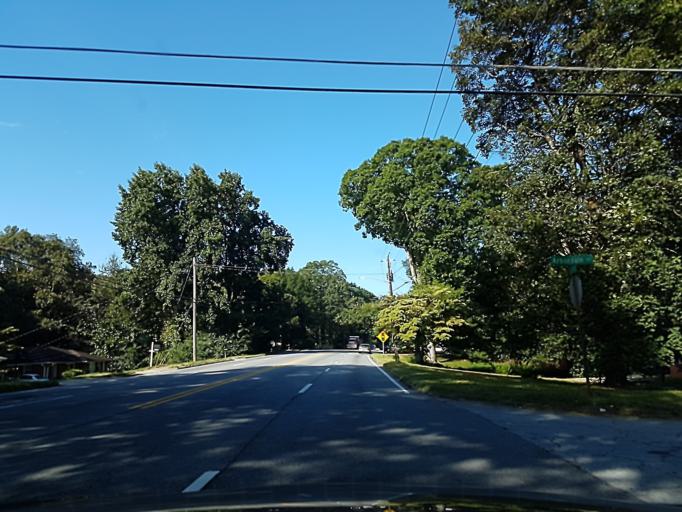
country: US
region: Georgia
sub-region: DeKalb County
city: North Druid Hills
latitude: 33.8109
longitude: -84.2875
